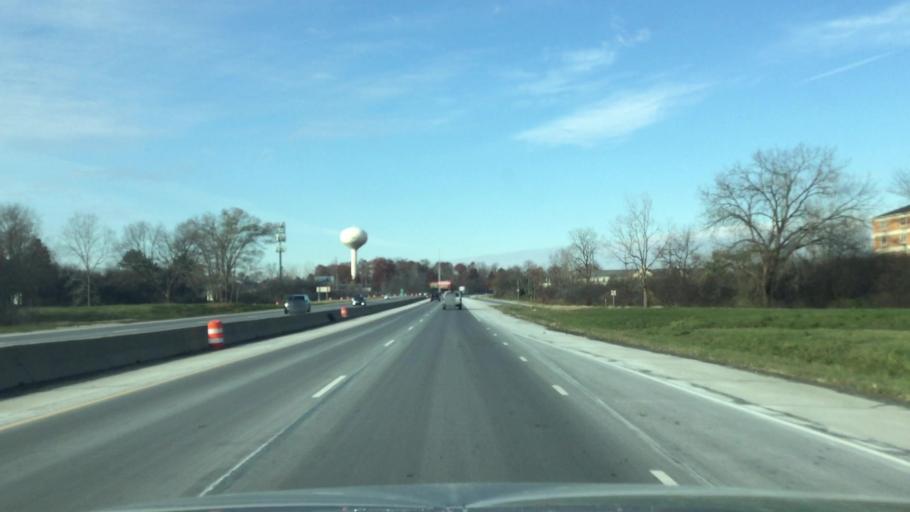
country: US
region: Michigan
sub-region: Washtenaw County
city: Ann Arbor
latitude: 42.2370
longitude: -83.7412
